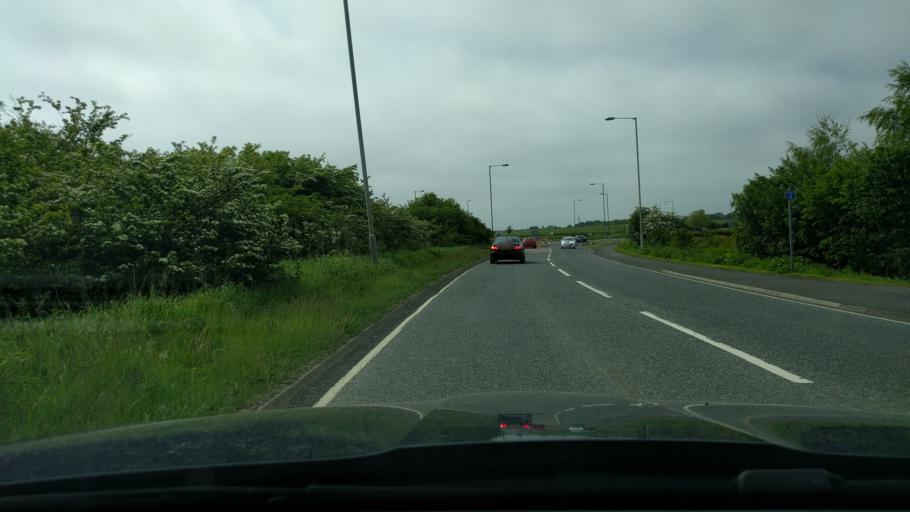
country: GB
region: England
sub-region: Northumberland
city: East Chevington
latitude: 55.2509
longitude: -1.6024
